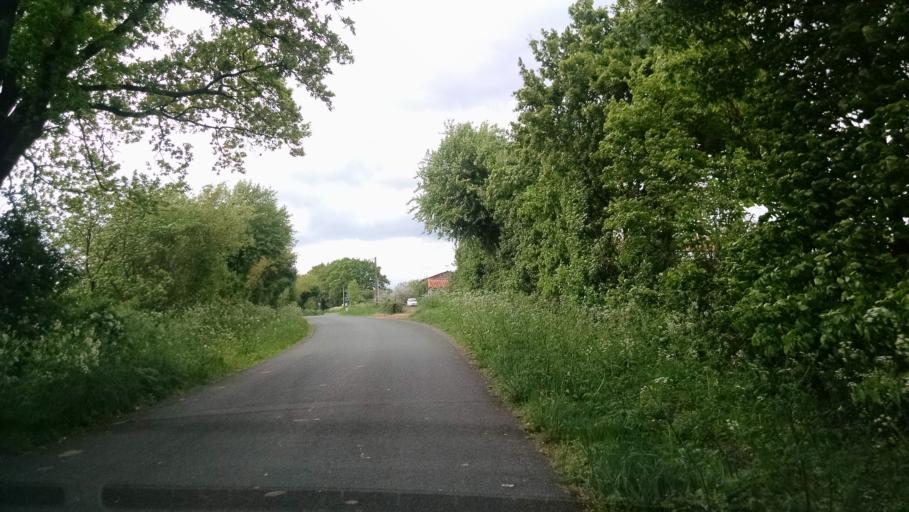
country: FR
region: Pays de la Loire
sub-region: Departement de la Vendee
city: Saint-Hilaire-de-Loulay
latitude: 46.9864
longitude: -1.3390
